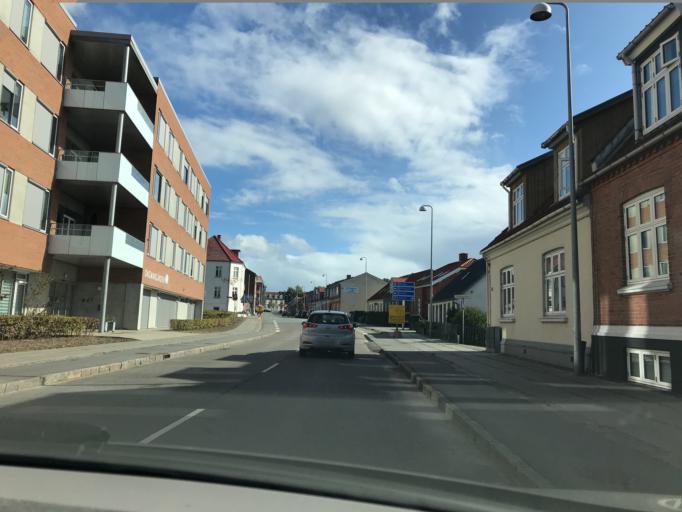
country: DK
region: Central Jutland
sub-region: Skanderborg Kommune
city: Skanderborg
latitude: 56.0329
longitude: 9.9274
